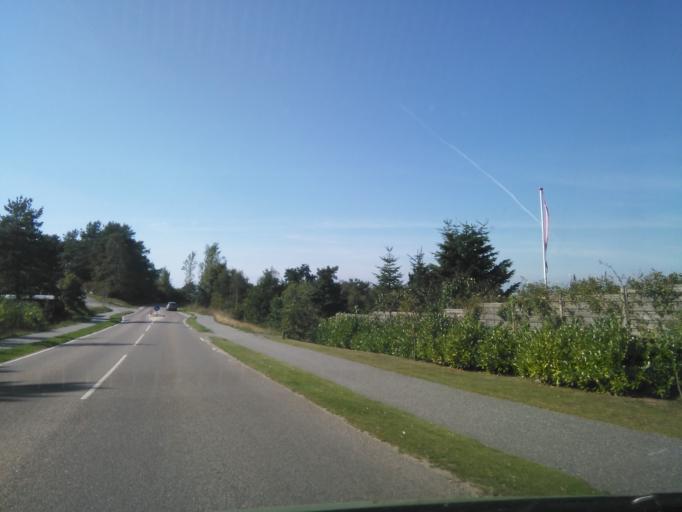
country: DK
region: Central Jutland
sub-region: Syddjurs Kommune
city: Ebeltoft
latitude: 56.2004
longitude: 10.6989
